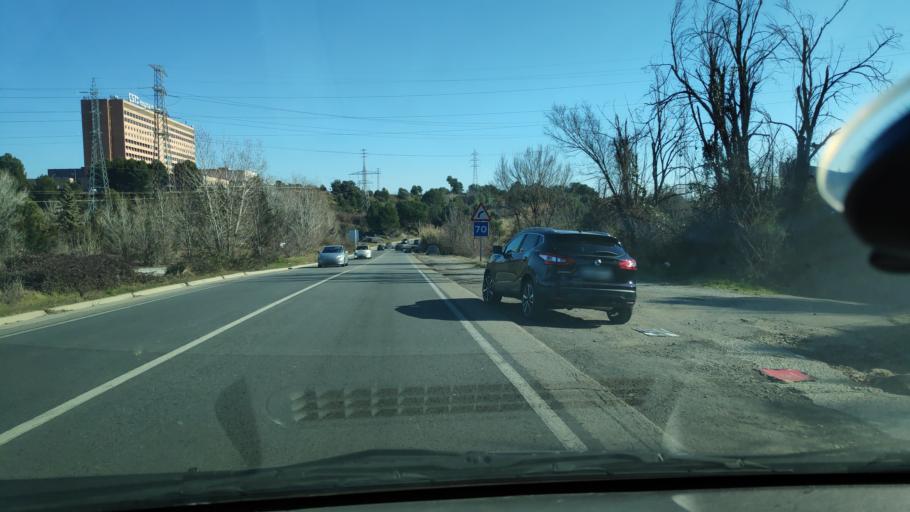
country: ES
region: Catalonia
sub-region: Provincia de Barcelona
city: Terrassa
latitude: 41.5562
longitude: 2.0478
